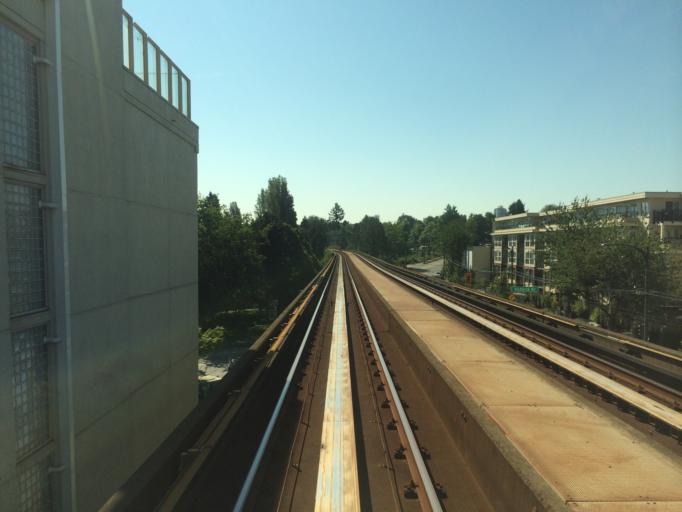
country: CA
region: British Columbia
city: Vancouver
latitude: 49.2533
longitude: -123.0666
